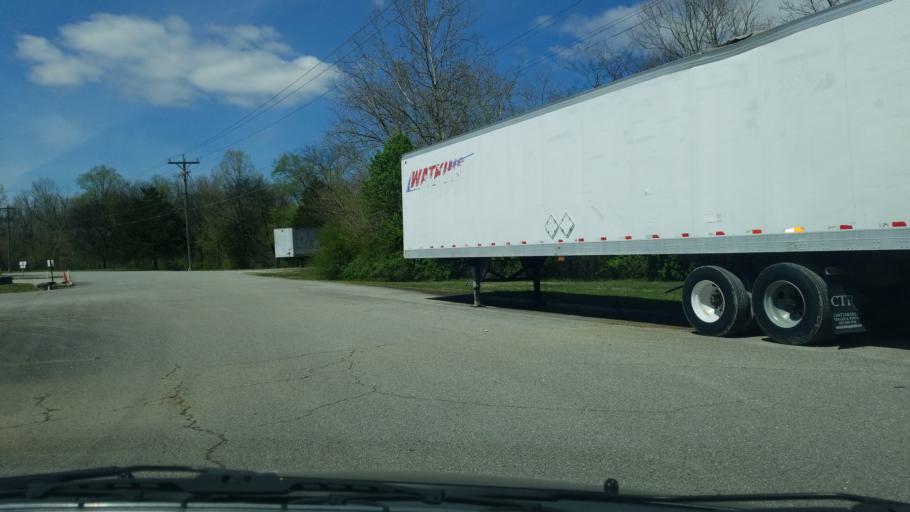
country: US
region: Tennessee
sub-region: Hamilton County
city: Collegedale
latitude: 35.0786
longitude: -85.0532
